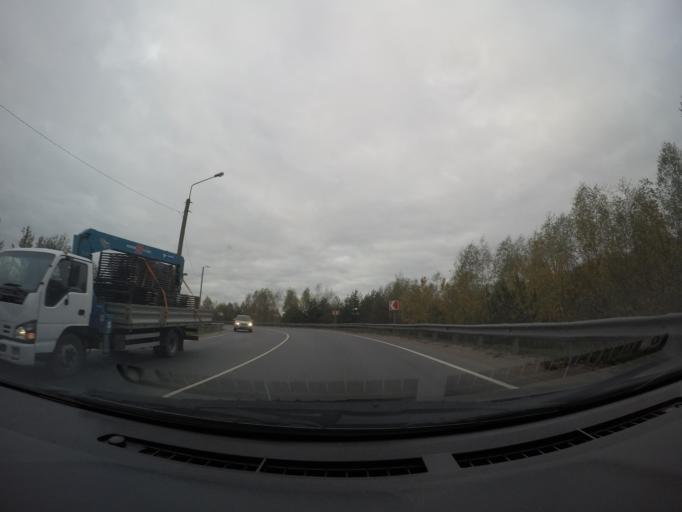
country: RU
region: Moskovskaya
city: Fryazevo
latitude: 55.7231
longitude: 38.4184
